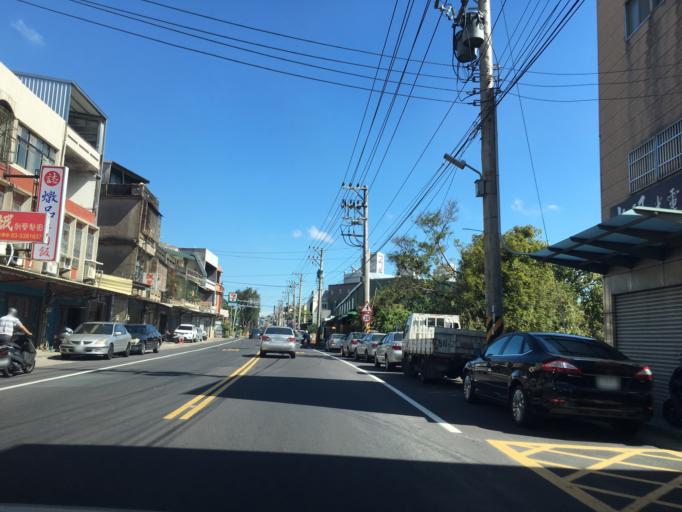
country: TW
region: Taiwan
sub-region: Hsinchu
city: Hsinchu
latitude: 24.8052
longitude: 120.9391
